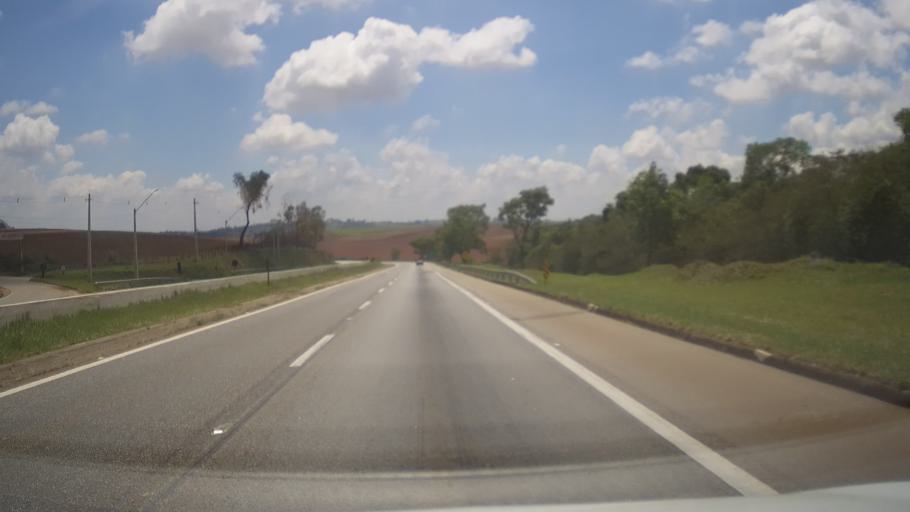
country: BR
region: Minas Gerais
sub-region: Sao Goncalo Do Sapucai
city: Sao Goncalo do Sapucai
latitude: -21.9395
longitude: -45.6158
